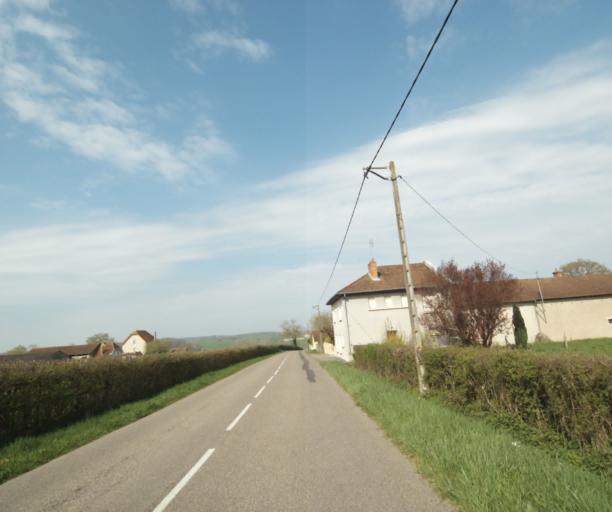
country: FR
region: Bourgogne
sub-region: Departement de Saone-et-Loire
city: Palinges
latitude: 46.5058
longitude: 4.1921
